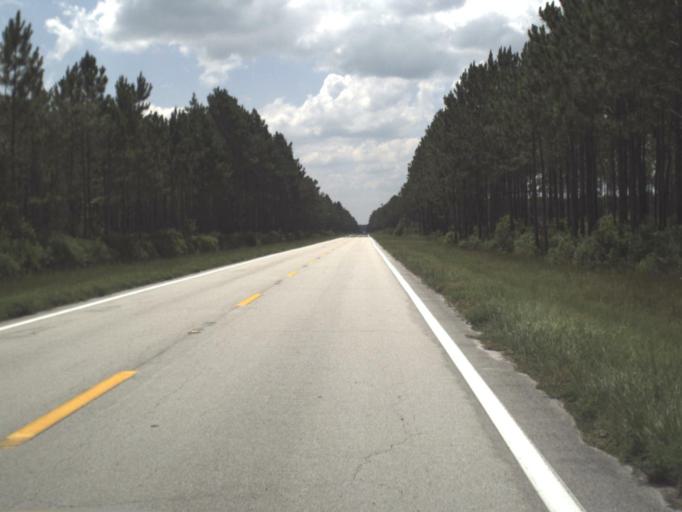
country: US
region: Florida
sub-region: Baker County
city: Macclenny
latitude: 30.5558
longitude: -82.3728
